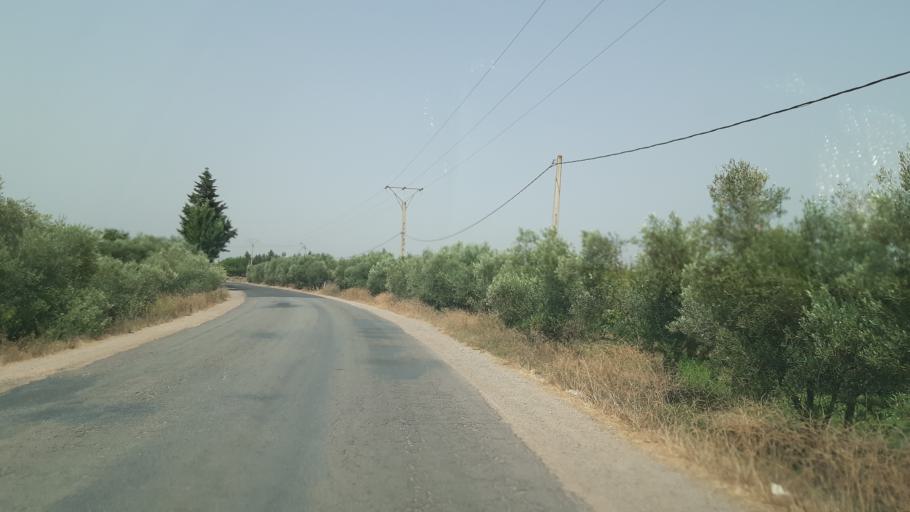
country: MA
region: Fes-Boulemane
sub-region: Fes
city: Oulad Tayeb
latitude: 33.8462
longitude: -5.1104
